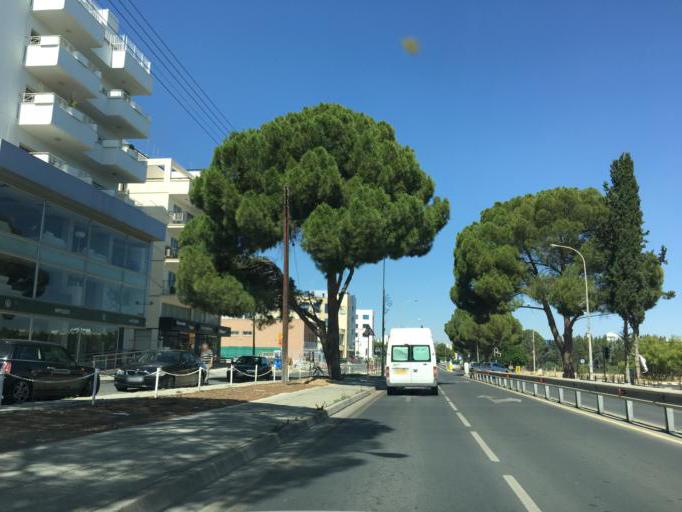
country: CY
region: Lefkosia
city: Nicosia
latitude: 35.1642
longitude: 33.3251
